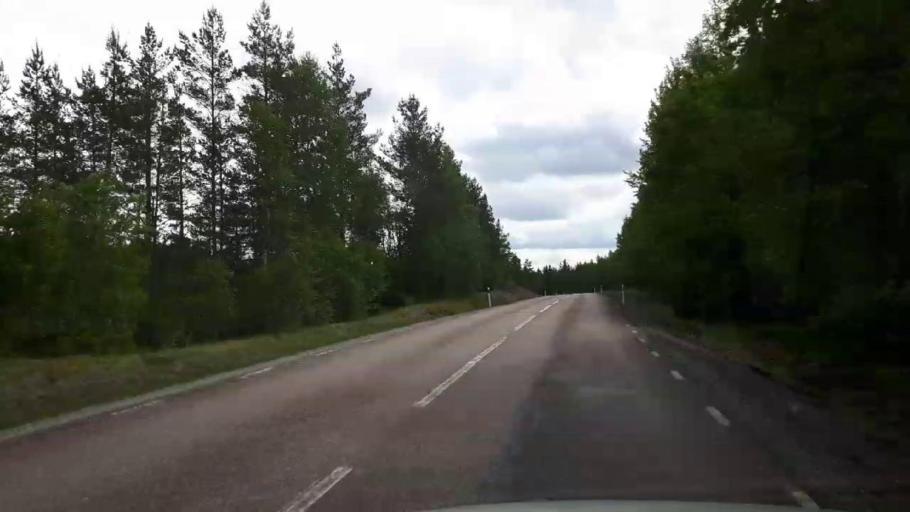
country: SE
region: Vaestmanland
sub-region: Fagersta Kommun
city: Fagersta
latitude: 59.8858
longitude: 15.8310
